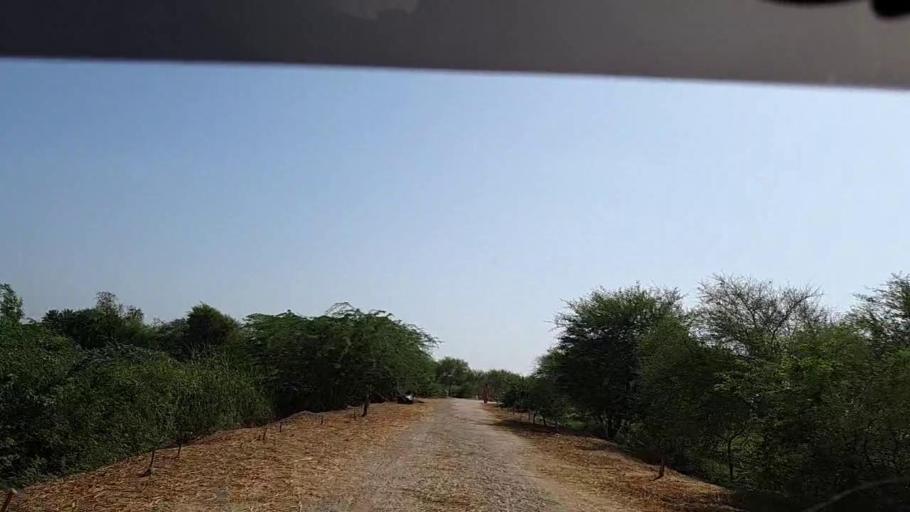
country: PK
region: Sindh
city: Badin
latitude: 24.6346
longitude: 68.7863
